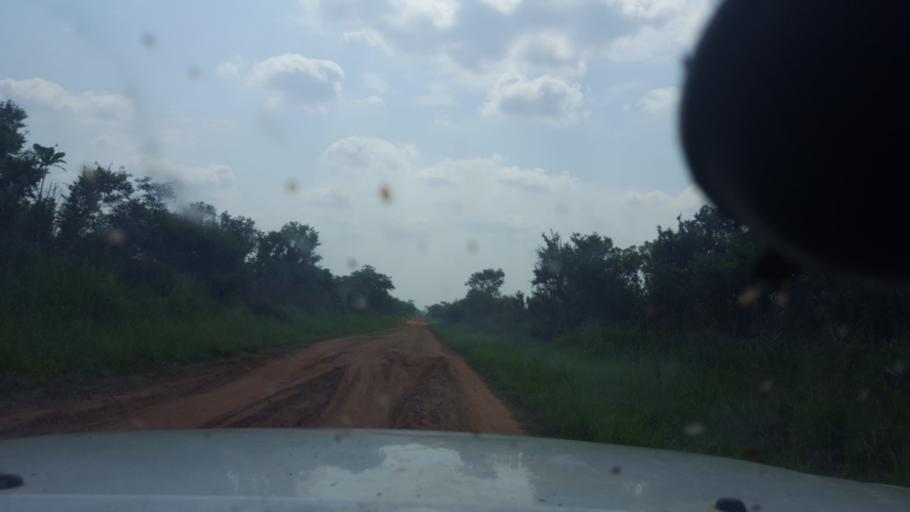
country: CD
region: Bandundu
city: Bandundu
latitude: -3.7620
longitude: 17.1468
